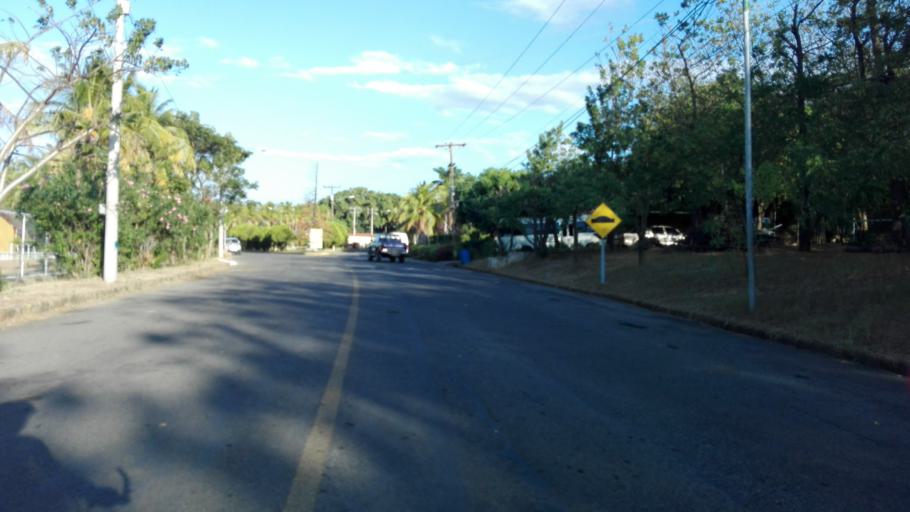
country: NI
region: Managua
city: Managua
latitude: 12.1148
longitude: -86.2465
